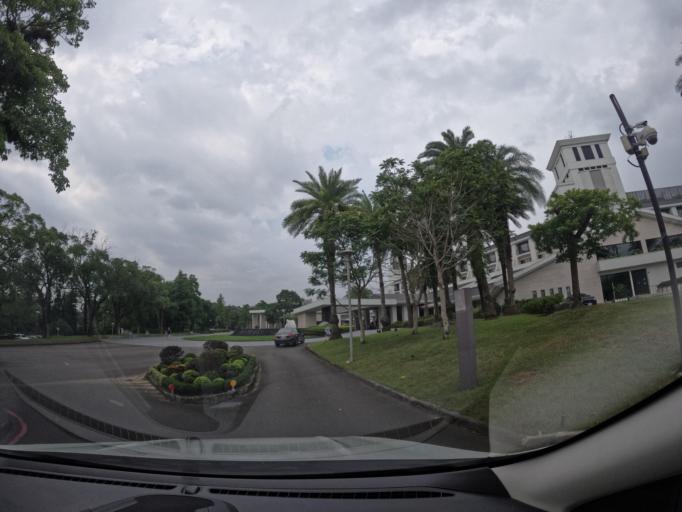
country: TW
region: Taiwan
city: Daxi
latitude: 24.8818
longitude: 121.3260
